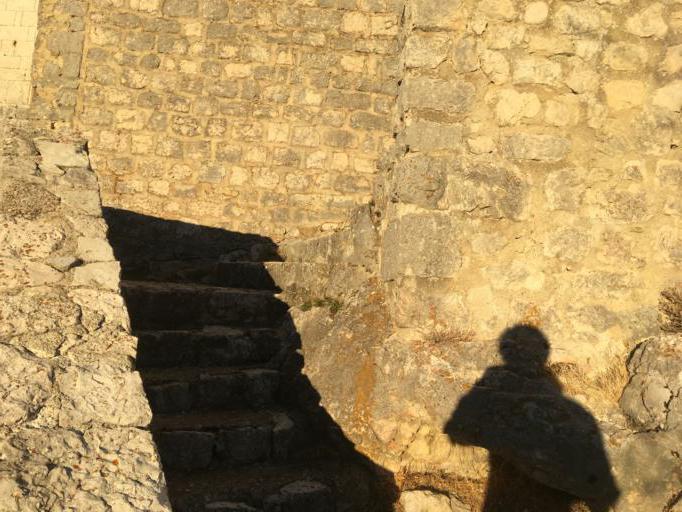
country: FR
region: Provence-Alpes-Cote d'Azur
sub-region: Departement du Var
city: Bargemon
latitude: 43.7103
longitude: 6.5110
